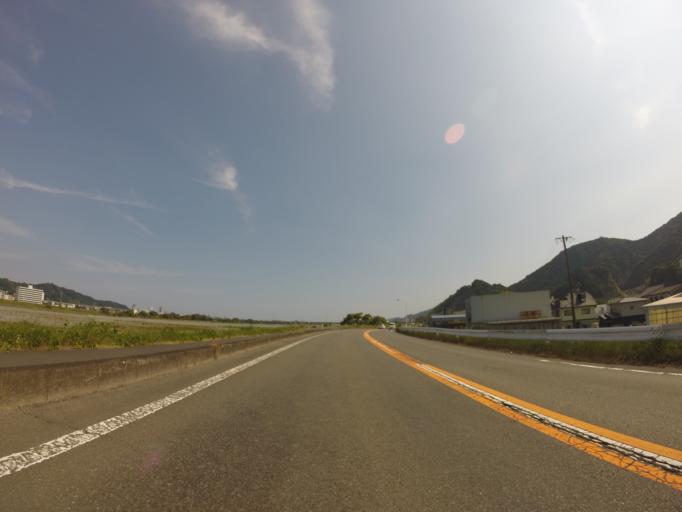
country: JP
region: Shizuoka
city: Shizuoka-shi
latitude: 34.9969
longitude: 138.3549
